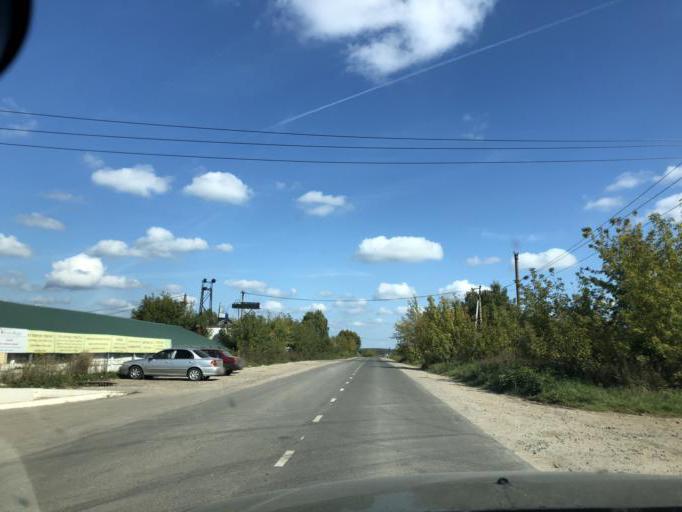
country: RU
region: Tula
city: Yasnogorsk
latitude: 54.4898
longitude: 37.6894
